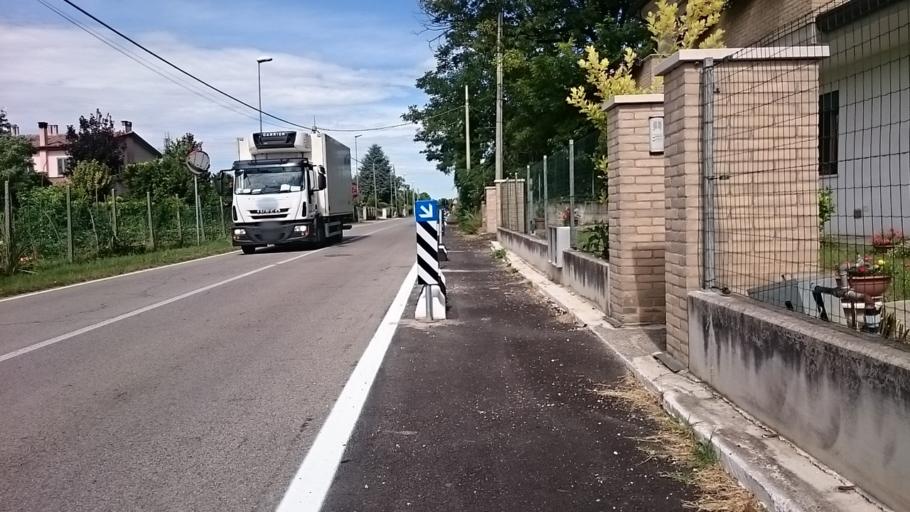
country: IT
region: Veneto
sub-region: Provincia di Padova
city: Albignasego
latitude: 45.3503
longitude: 11.8941
